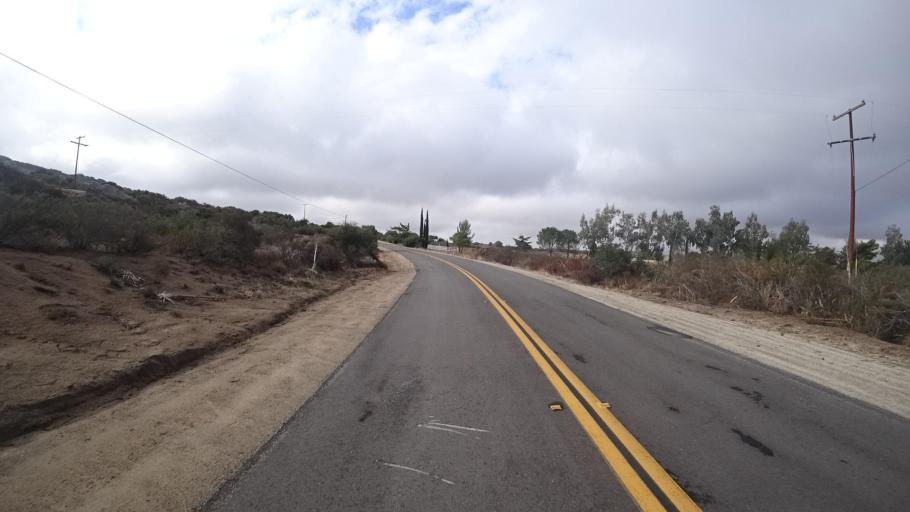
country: MX
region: Baja California
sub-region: Tecate
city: Hacienda Tecate
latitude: 32.6181
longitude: -116.5687
